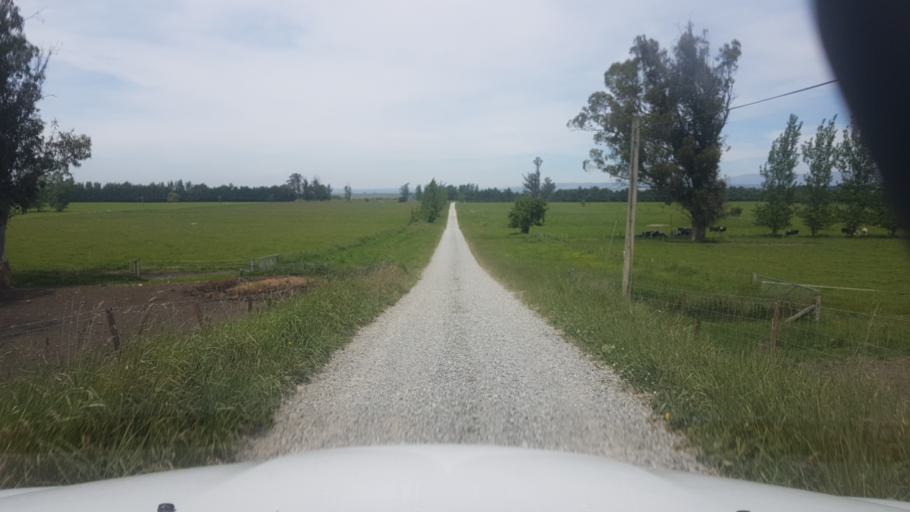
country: NZ
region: Canterbury
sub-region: Timaru District
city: Pleasant Point
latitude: -44.1969
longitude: 171.0910
